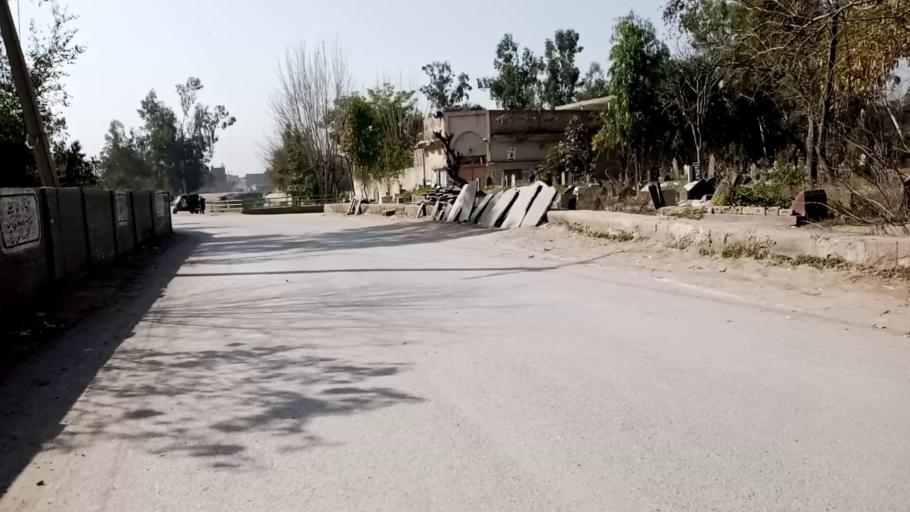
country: PK
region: Khyber Pakhtunkhwa
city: Peshawar
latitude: 33.9962
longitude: 71.5857
